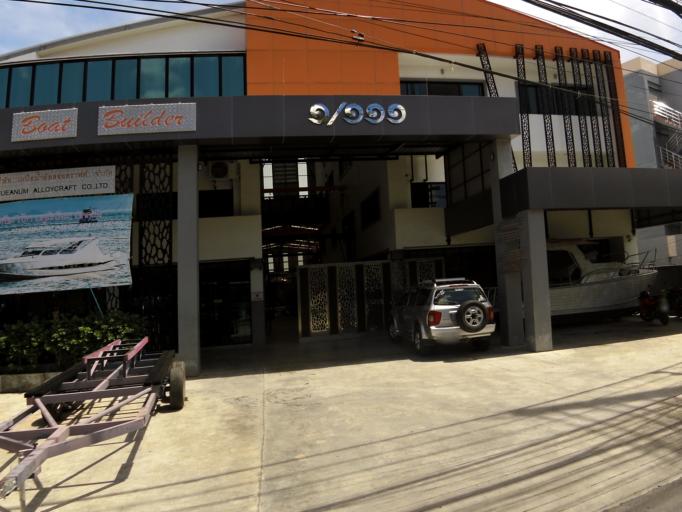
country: TH
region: Phuket
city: Ban Chalong
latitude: 7.8618
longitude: 98.3443
